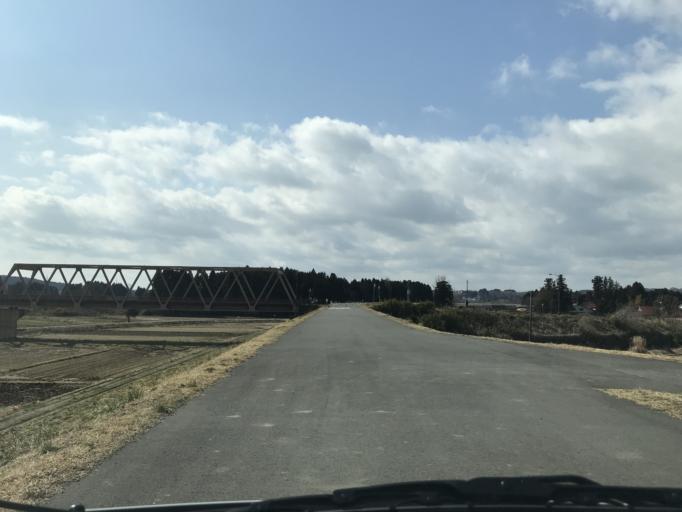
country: JP
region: Iwate
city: Mizusawa
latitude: 39.0429
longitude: 141.1447
